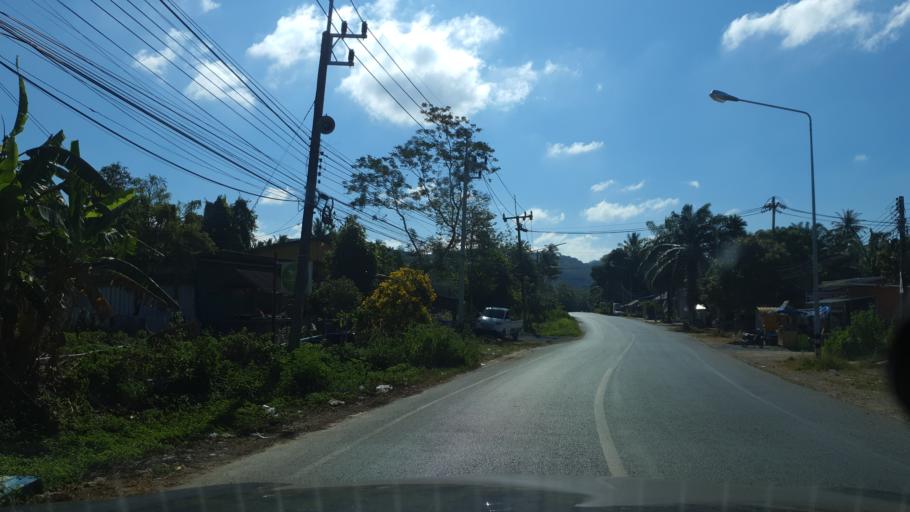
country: TH
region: Phangnga
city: Ban Ao Nang
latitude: 8.0631
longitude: 98.8118
